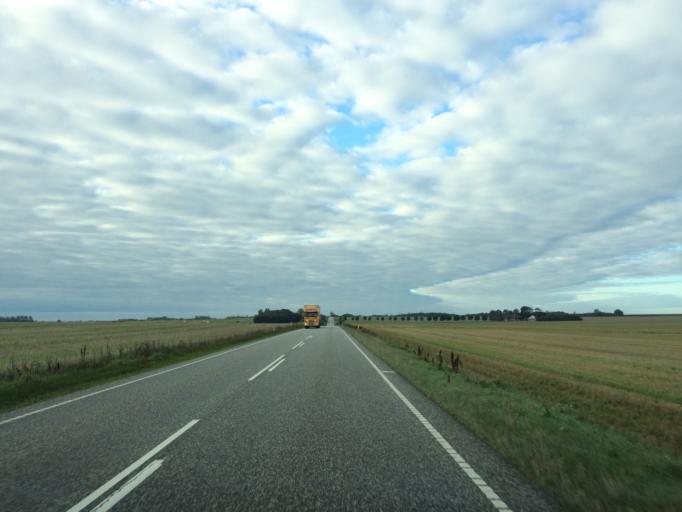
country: DK
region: Central Jutland
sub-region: Ringkobing-Skjern Kommune
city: Skjern
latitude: 56.0437
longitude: 8.5035
